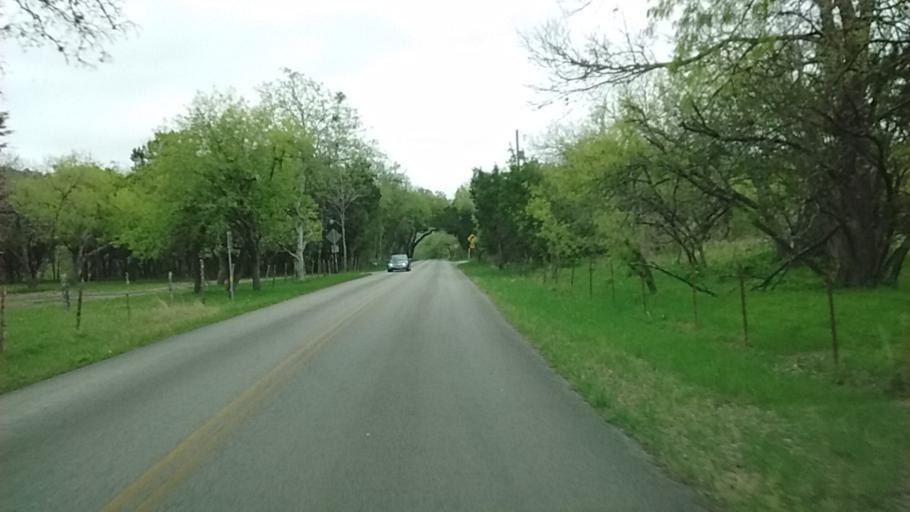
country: US
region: Texas
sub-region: Comal County
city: New Braunfels
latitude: 29.8016
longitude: -98.1714
